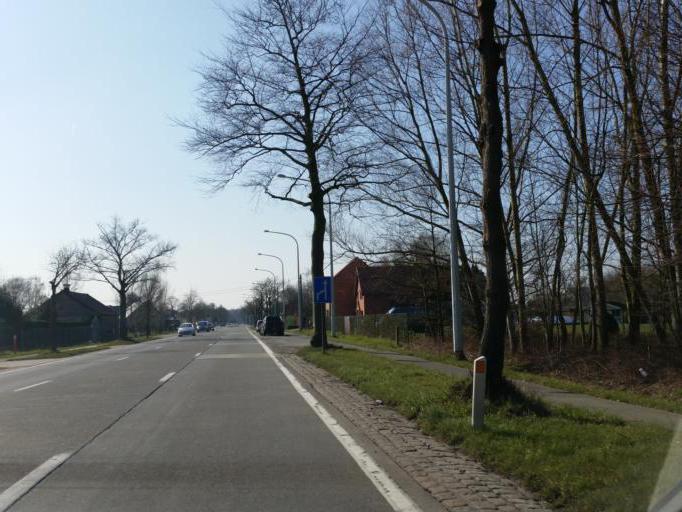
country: BE
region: Flanders
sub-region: Provincie Oost-Vlaanderen
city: Lokeren
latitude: 51.1201
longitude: 4.0230
